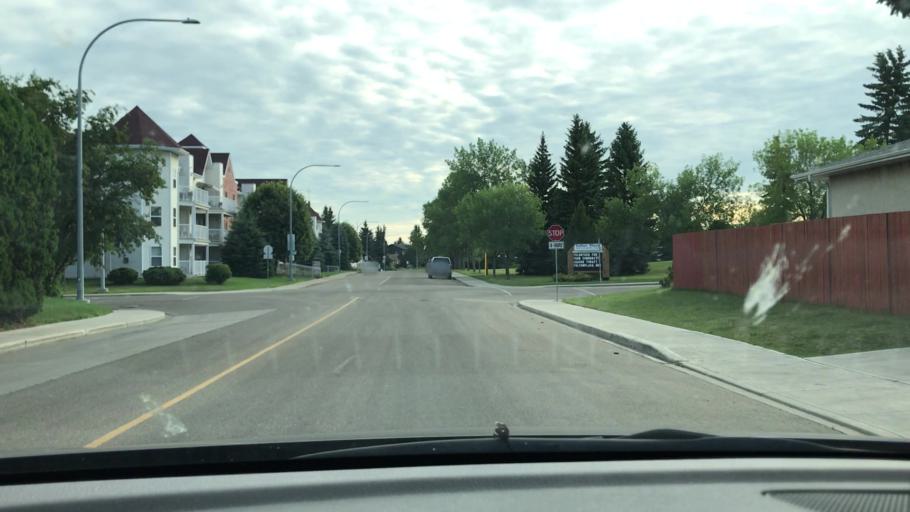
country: CA
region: Alberta
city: Edmonton
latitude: 53.5449
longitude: -113.4281
